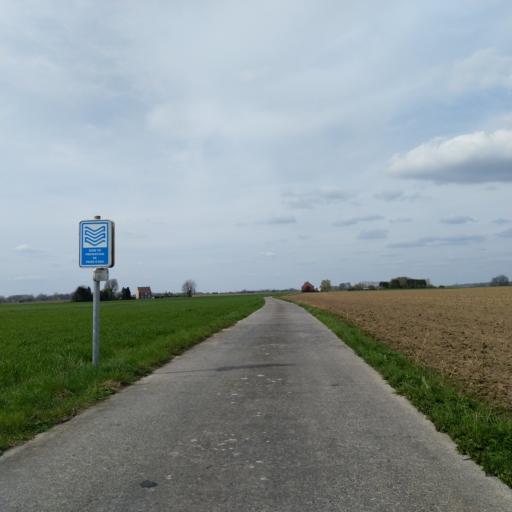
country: BE
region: Wallonia
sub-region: Province du Hainaut
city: Jurbise
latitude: 50.5393
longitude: 3.9237
